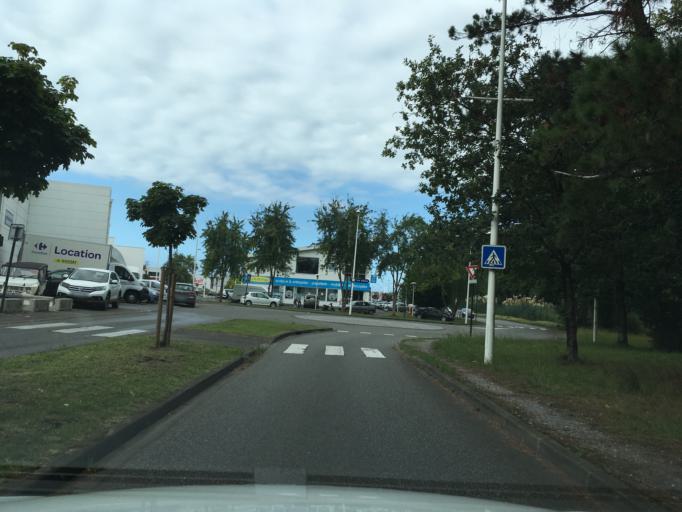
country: FR
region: Aquitaine
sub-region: Departement des Pyrenees-Atlantiques
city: Bayonne
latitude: 43.4901
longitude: -1.4909
